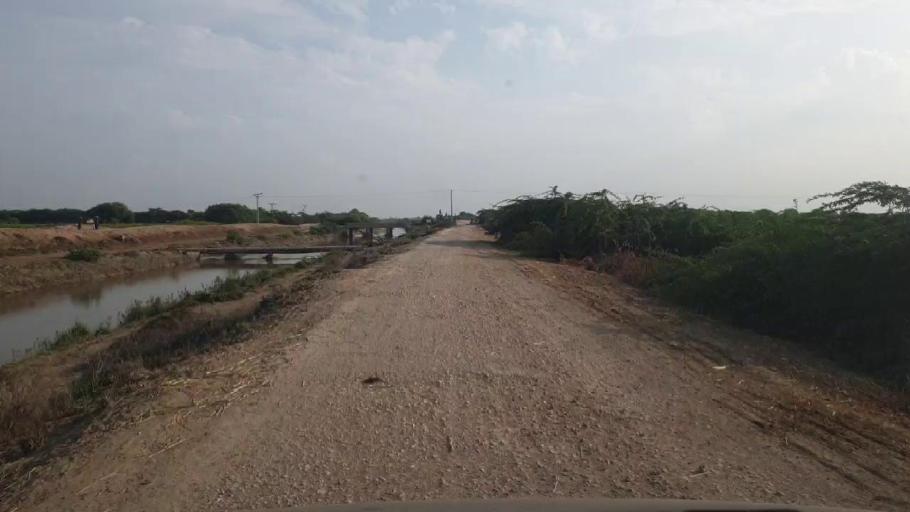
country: PK
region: Sindh
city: Badin
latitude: 24.5511
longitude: 68.6707
